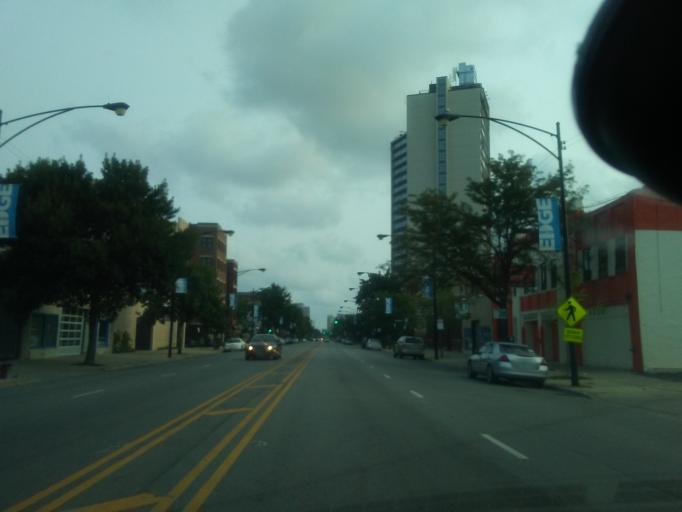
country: US
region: Illinois
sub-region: Cook County
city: Evanston
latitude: 41.9863
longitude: -87.6601
